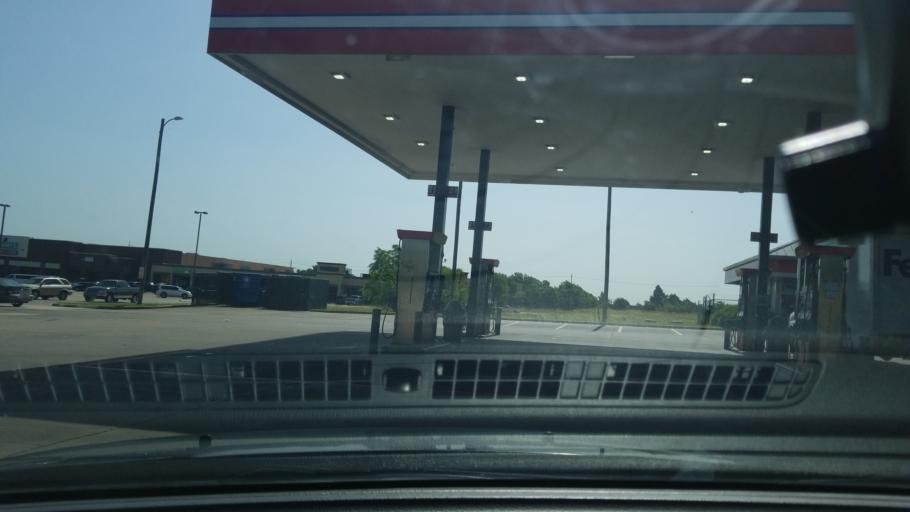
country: US
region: Texas
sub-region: Dallas County
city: Mesquite
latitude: 32.8041
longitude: -96.6822
